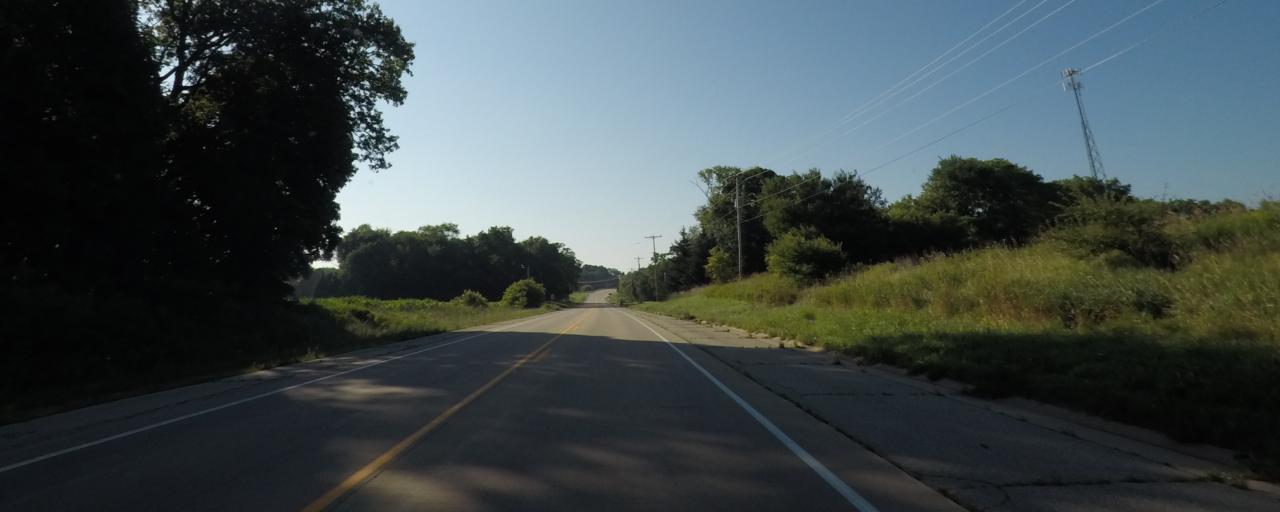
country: US
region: Wisconsin
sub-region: Jefferson County
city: Lake Koshkonong
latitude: 42.9583
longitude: -88.8899
